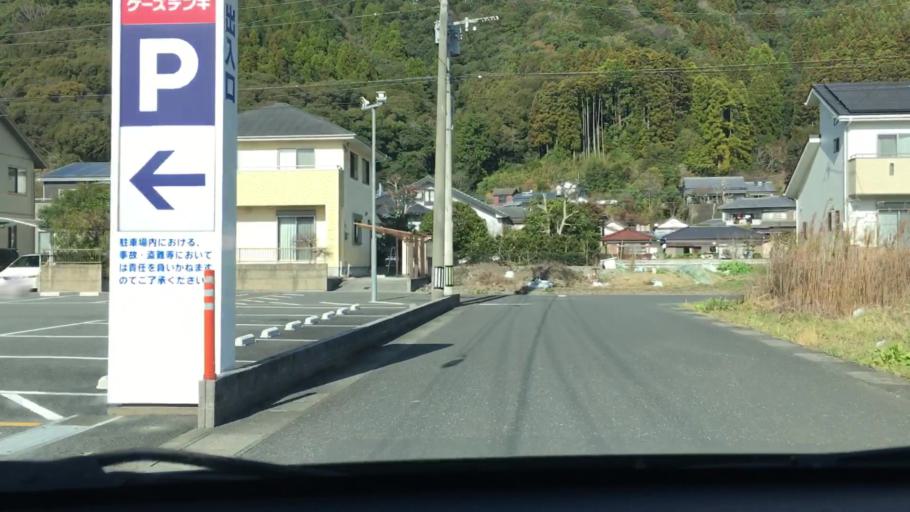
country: JP
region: Oita
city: Saiki
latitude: 32.9626
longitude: 131.8681
